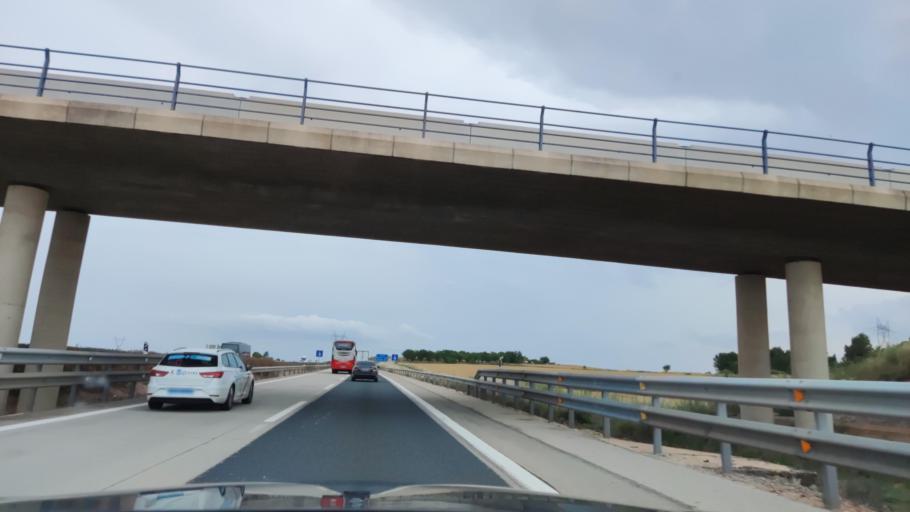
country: ES
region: Castille-La Mancha
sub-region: Provincia de Cuenca
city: Honrubia
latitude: 39.6099
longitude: -2.2891
